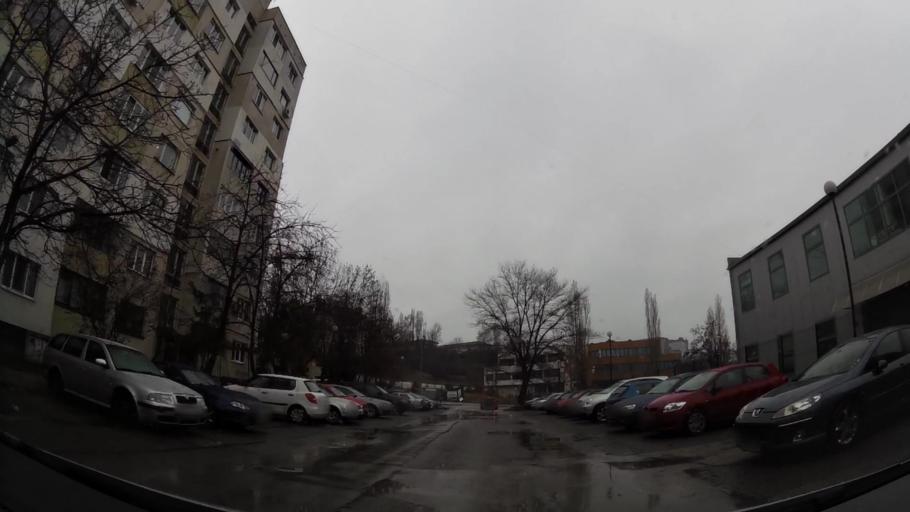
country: BG
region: Sofia-Capital
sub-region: Stolichna Obshtina
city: Sofia
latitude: 42.6540
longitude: 23.3963
